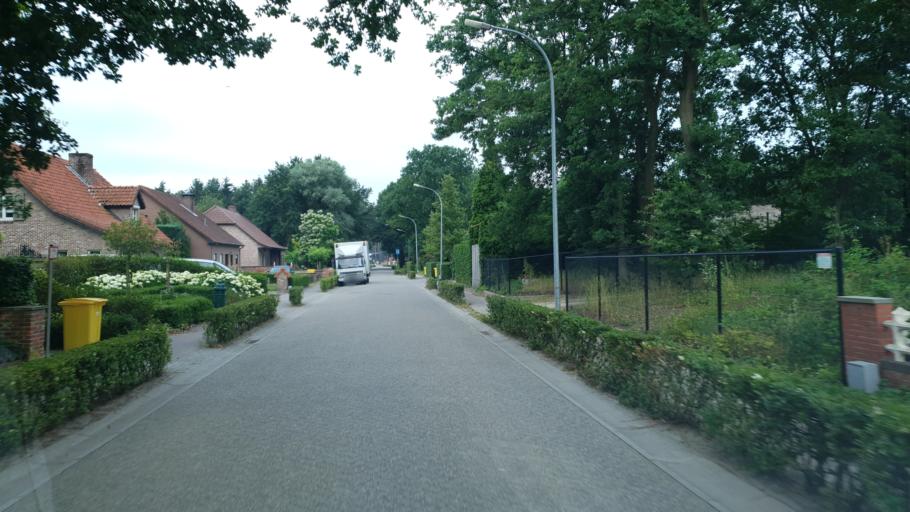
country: BE
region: Flanders
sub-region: Provincie Antwerpen
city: Merksplas
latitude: 51.3663
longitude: 4.8474
